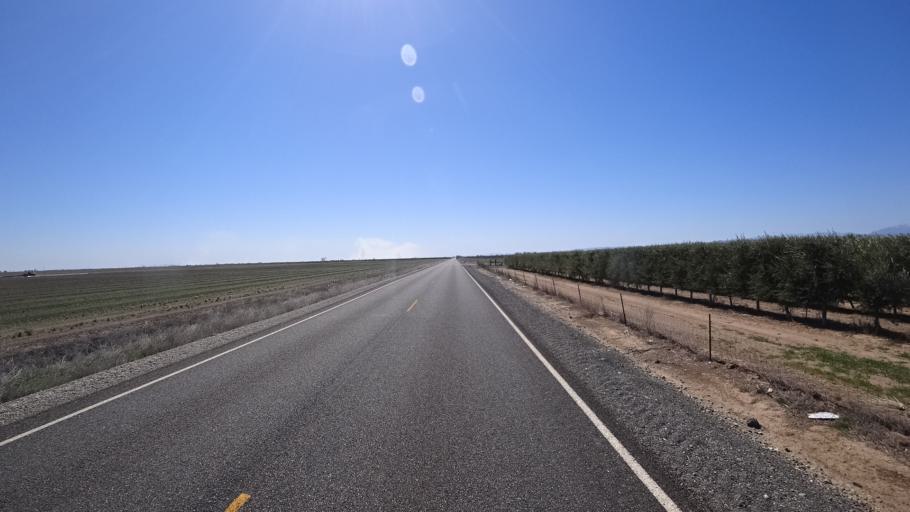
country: US
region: California
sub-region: Glenn County
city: Willows
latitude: 39.5908
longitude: -122.2499
